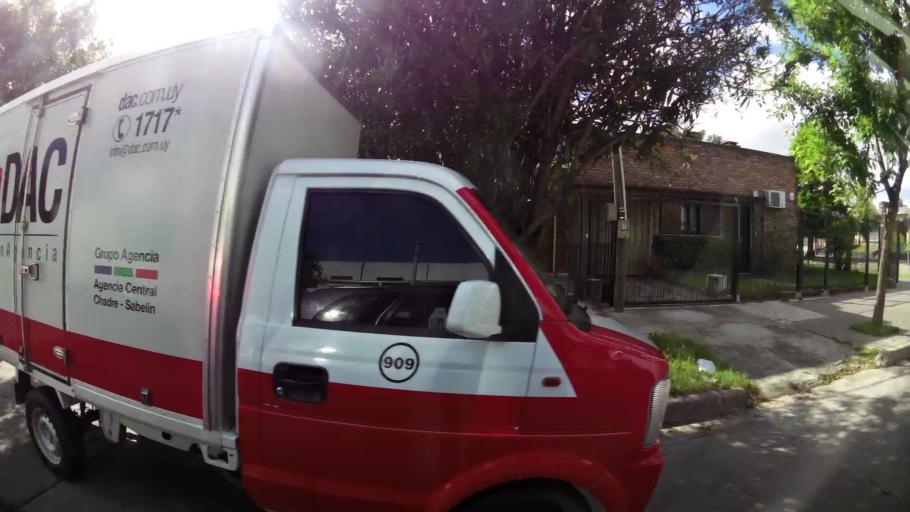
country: UY
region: Montevideo
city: Montevideo
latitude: -34.8785
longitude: -56.1630
